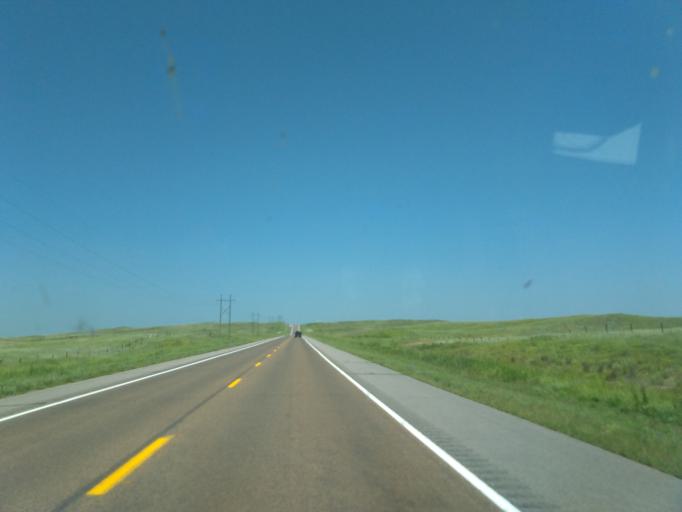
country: US
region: Nebraska
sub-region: Lincoln County
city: North Platte
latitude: 40.8632
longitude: -100.7541
